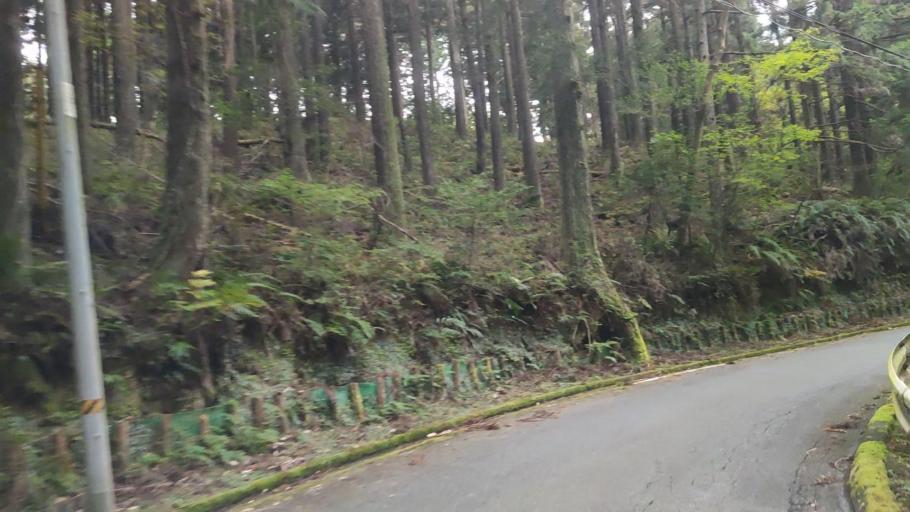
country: JP
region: Shizuoka
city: Ito
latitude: 34.9014
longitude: 138.9559
